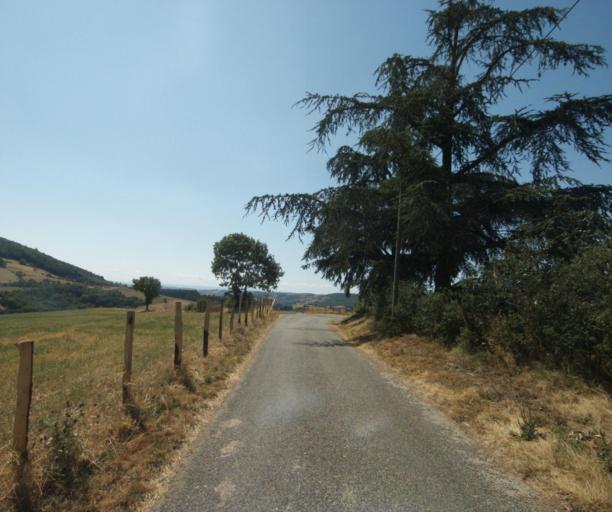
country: FR
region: Rhone-Alpes
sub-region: Departement du Rhone
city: Sainte-Foy-l'Argentiere
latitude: 45.7172
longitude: 4.5230
